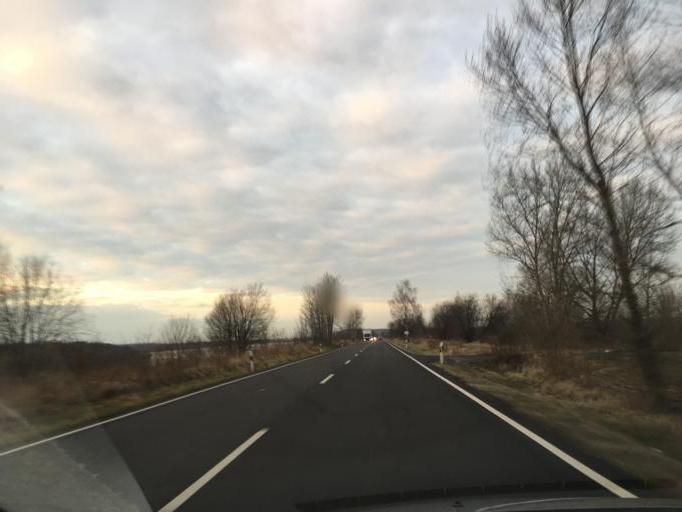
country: DE
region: Saxony
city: Espenhain
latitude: 51.2063
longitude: 12.4535
